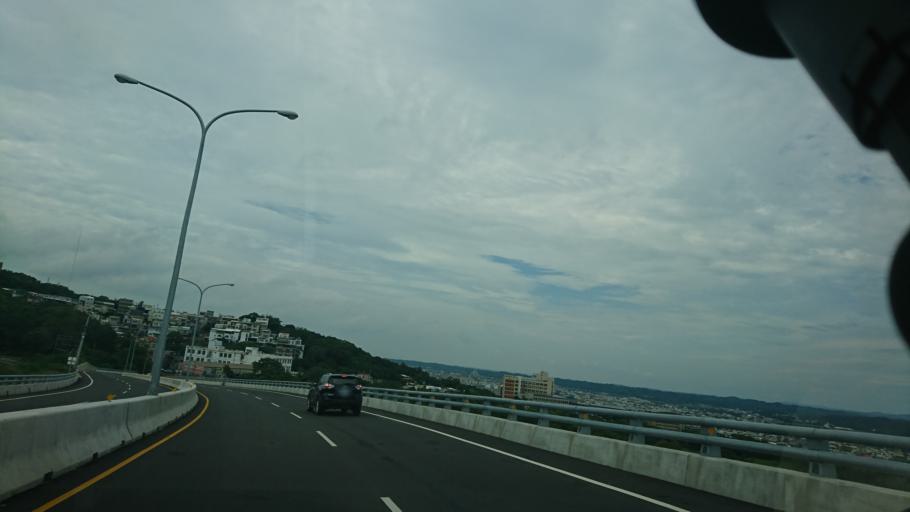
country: TW
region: Taiwan
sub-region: Miaoli
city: Miaoli
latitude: 24.5401
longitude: 120.8092
